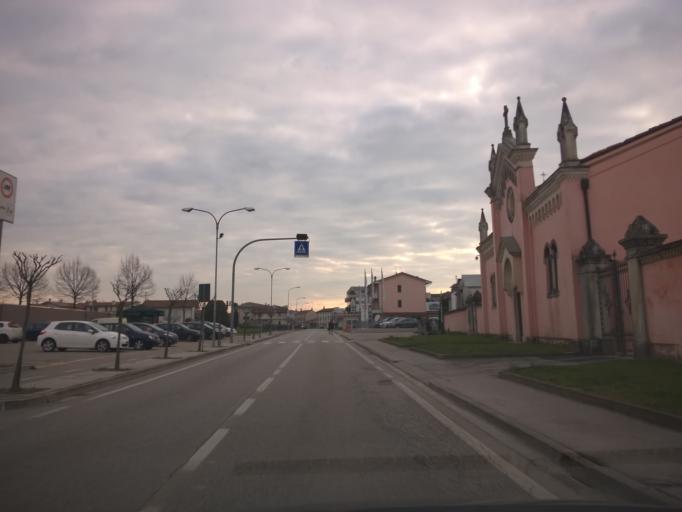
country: IT
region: Veneto
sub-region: Provincia di Vicenza
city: Dueville
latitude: 45.6398
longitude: 11.5488
